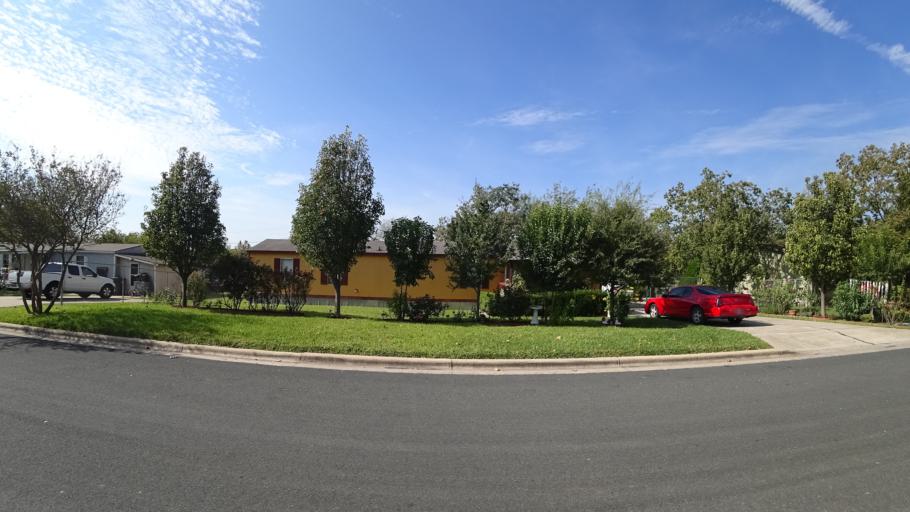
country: US
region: Texas
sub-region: Travis County
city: Pflugerville
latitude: 30.4106
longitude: -97.6303
